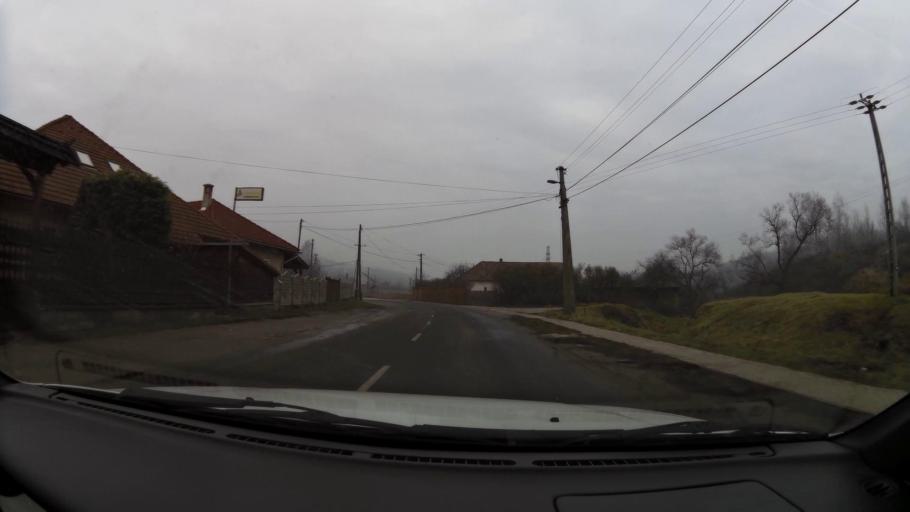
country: HU
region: Borsod-Abauj-Zemplen
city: Izsofalva
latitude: 48.3373
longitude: 20.6478
